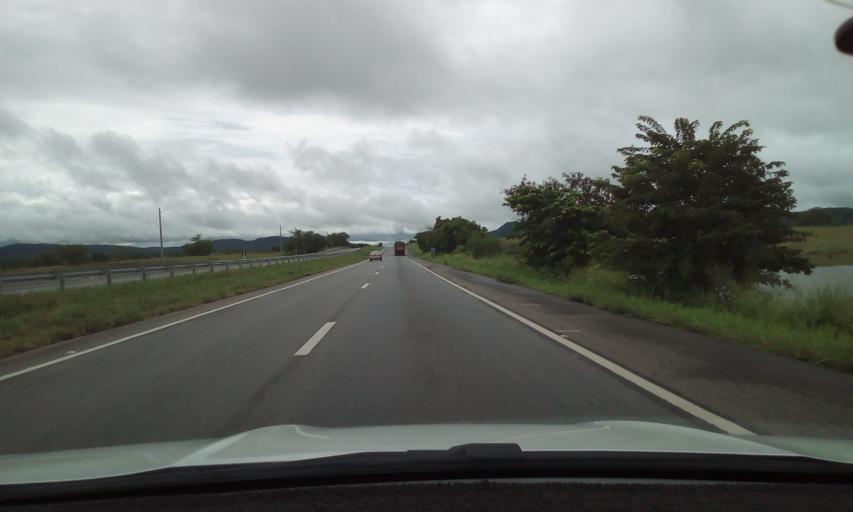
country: BR
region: Paraiba
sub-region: Gurinhem
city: Gurinhem
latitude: -7.1899
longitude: -35.4659
